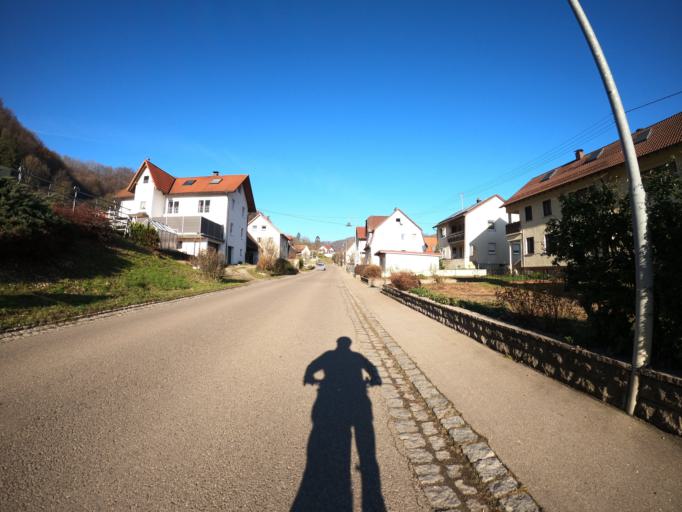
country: DE
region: Baden-Wuerttemberg
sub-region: Regierungsbezirk Stuttgart
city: Bad Ditzenbach
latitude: 48.6118
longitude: 9.6785
